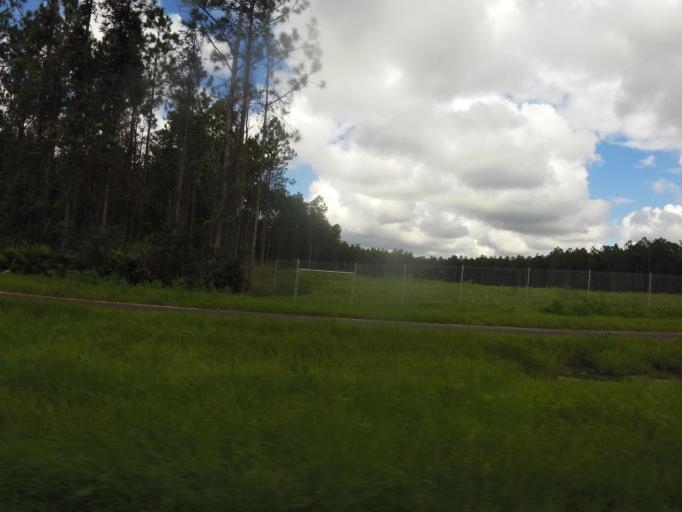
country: US
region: Florida
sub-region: Saint Johns County
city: Palm Valley
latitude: 30.0504
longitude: -81.3977
